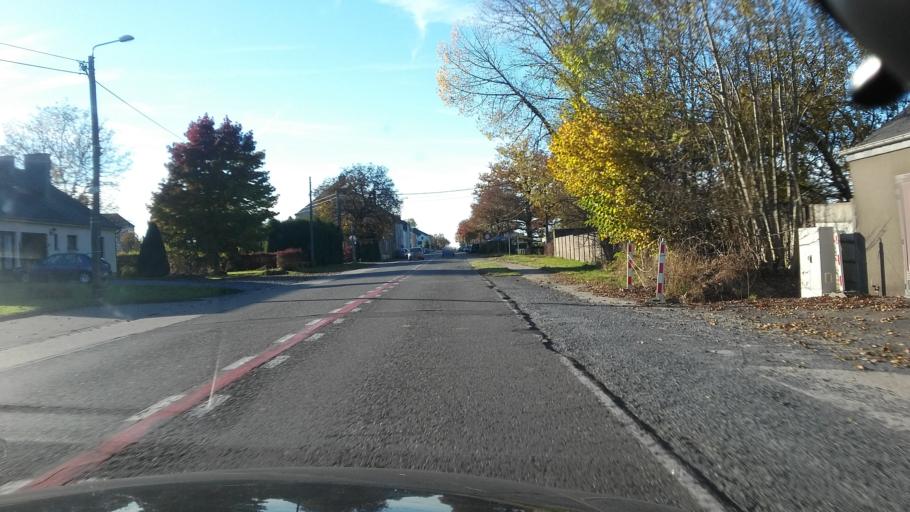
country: BE
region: Wallonia
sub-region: Province du Luxembourg
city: Etalle
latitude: 49.6746
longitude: 5.5666
